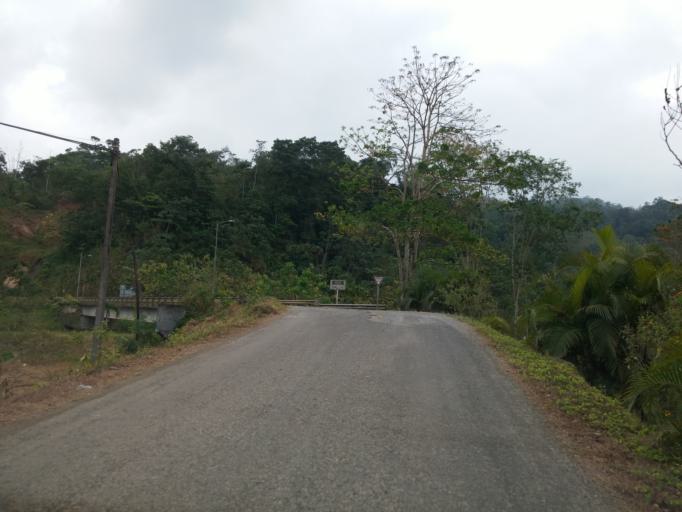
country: CR
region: Alajuela
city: Quesada
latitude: 10.3089
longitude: -84.5249
